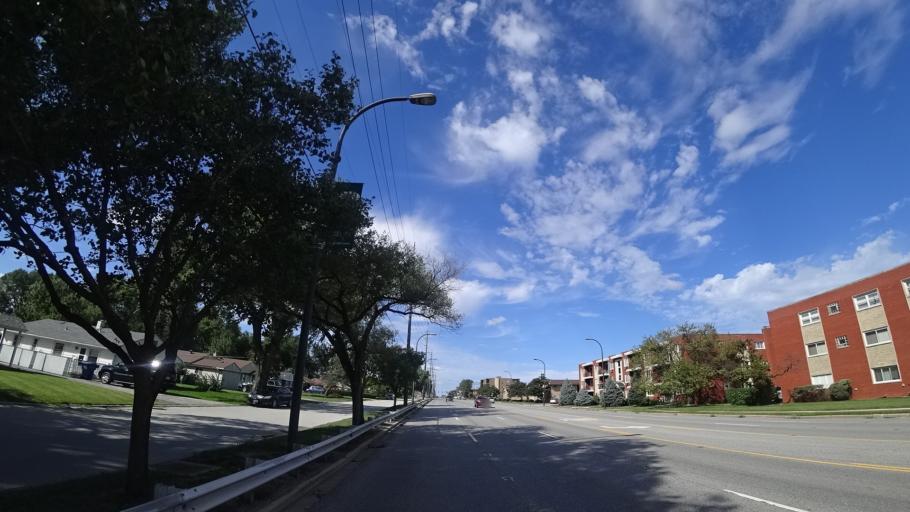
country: US
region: Illinois
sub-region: Cook County
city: Oak Lawn
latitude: 41.7095
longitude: -87.7405
